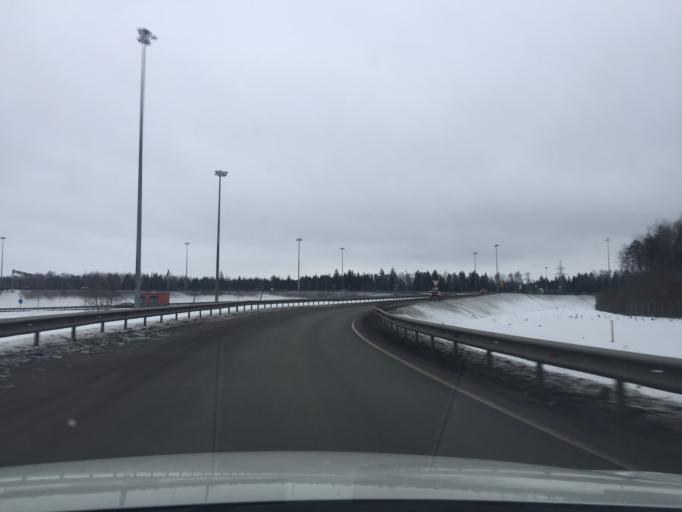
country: RU
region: St.-Petersburg
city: Krasnogvargeisky
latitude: 59.9459
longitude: 30.5360
